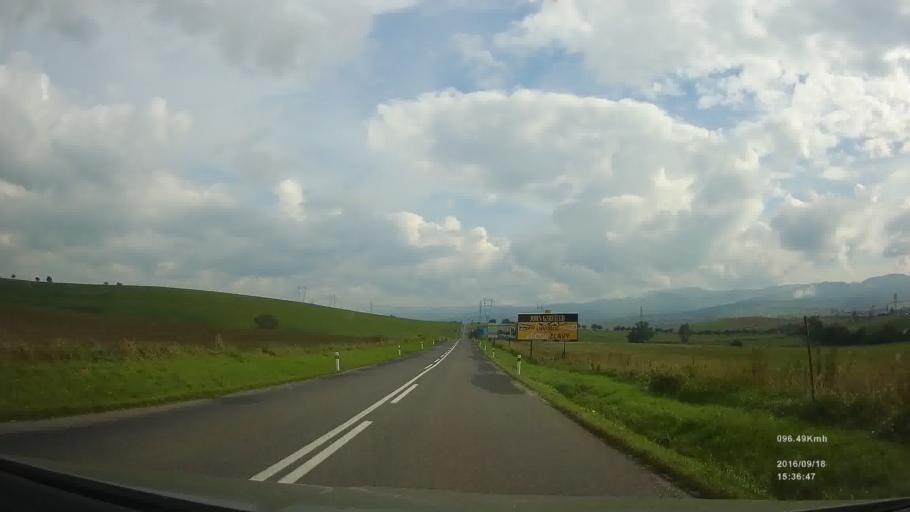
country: SK
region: Kosicky
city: Spisska Nova Ves
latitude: 48.9923
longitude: 20.4740
